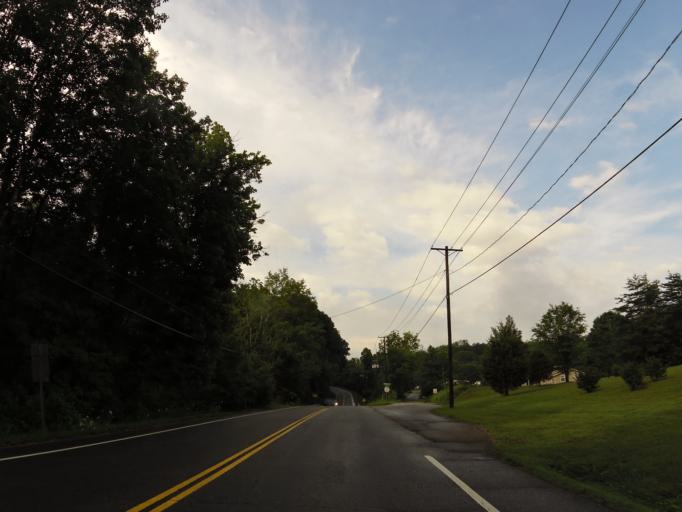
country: US
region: Tennessee
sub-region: Knox County
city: Knoxville
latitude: 35.8948
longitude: -83.9356
